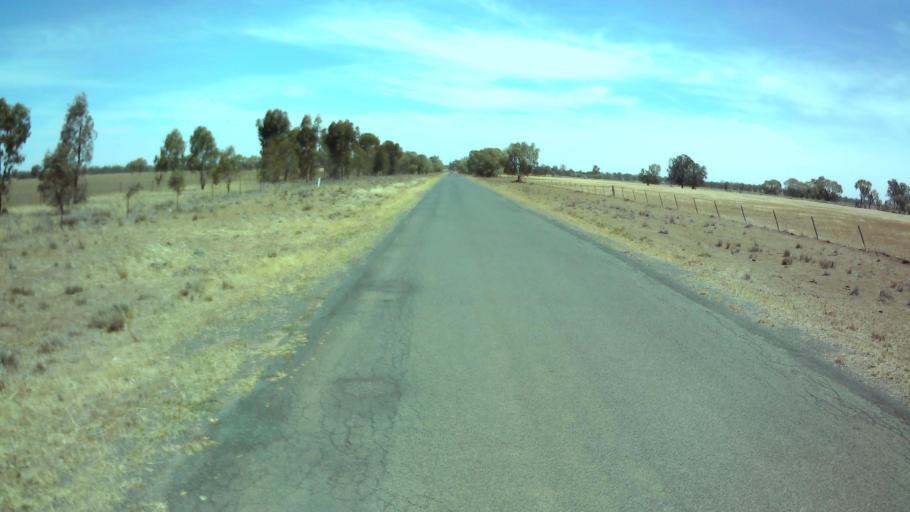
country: AU
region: New South Wales
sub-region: Weddin
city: Grenfell
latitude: -33.8234
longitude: 147.7471
